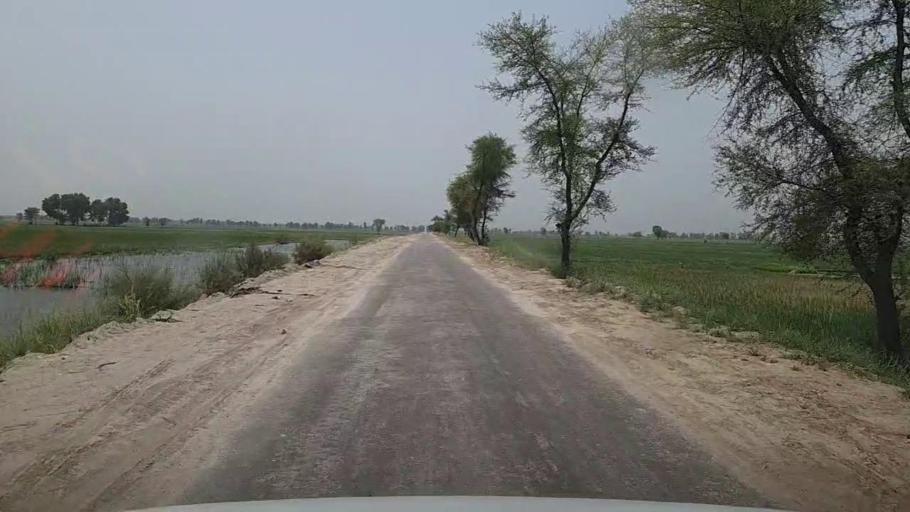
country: PK
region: Sindh
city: Sita Road
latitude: 27.0832
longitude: 67.9111
